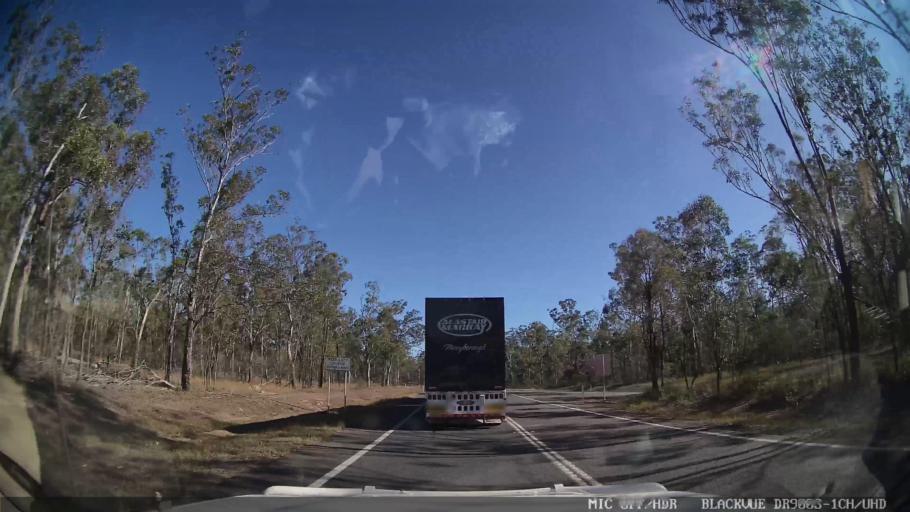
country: AU
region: Queensland
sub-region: Bundaberg
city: Childers
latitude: -25.2121
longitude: 152.0827
